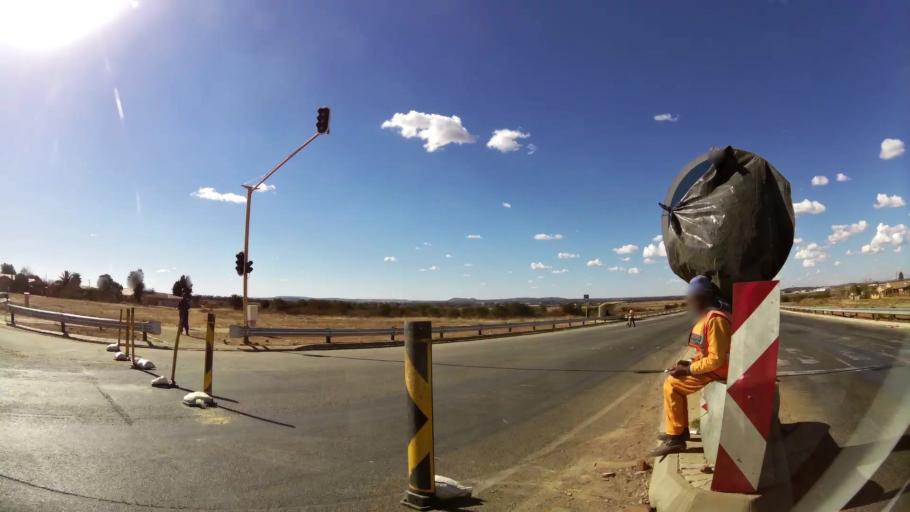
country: ZA
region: North-West
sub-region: Dr Kenneth Kaunda District Municipality
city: Klerksdorp
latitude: -26.8745
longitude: 26.5980
